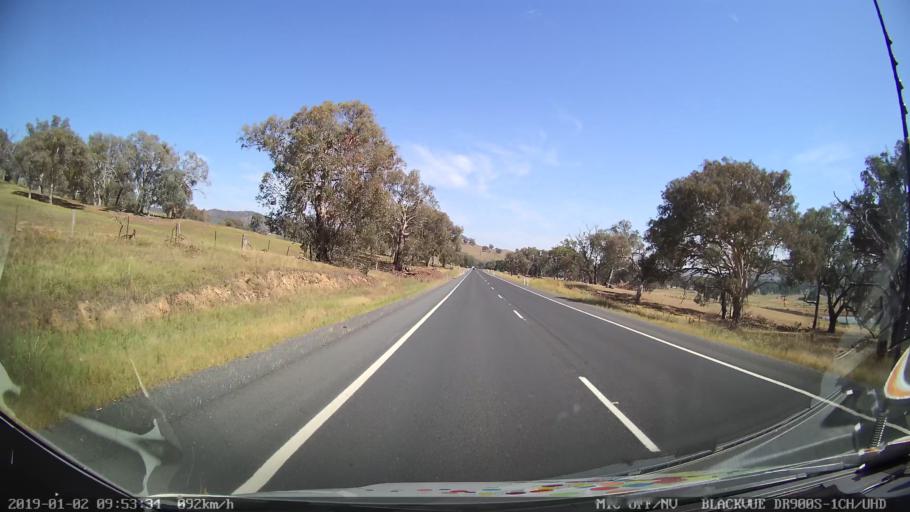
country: AU
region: New South Wales
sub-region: Tumut Shire
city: Tumut
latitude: -35.2464
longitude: 148.2019
